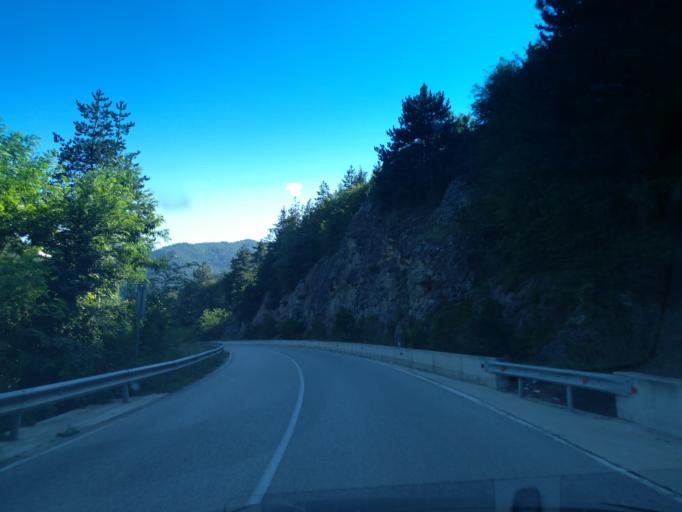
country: BG
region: Smolyan
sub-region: Obshtina Chepelare
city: Chepelare
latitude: 41.8543
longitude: 24.6846
